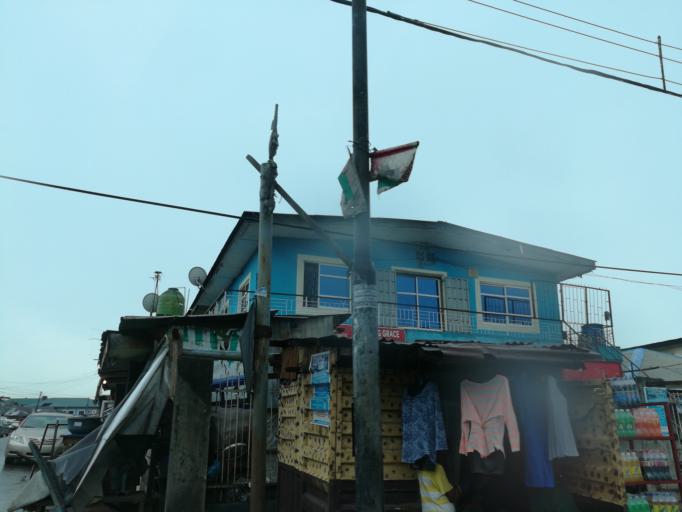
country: NG
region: Lagos
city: Oshodi
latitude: 6.5588
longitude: 3.3451
